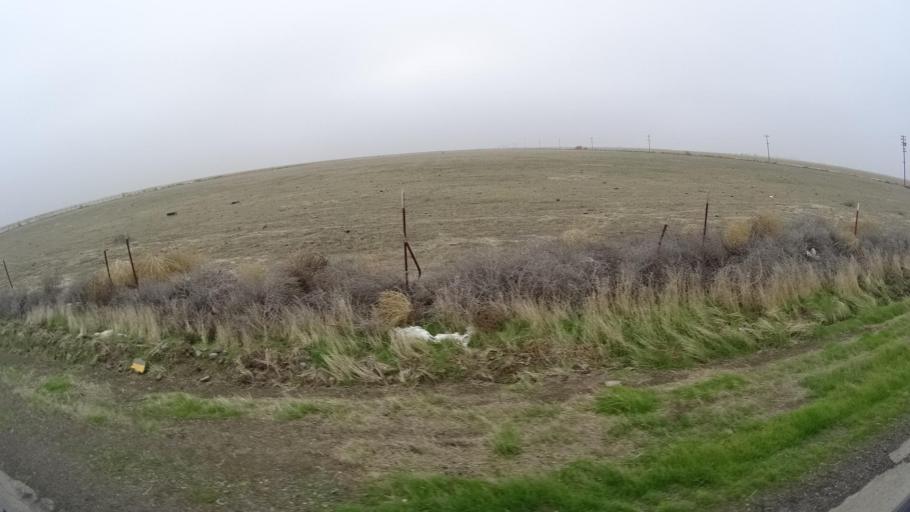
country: US
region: California
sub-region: Tulare County
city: Alpaugh
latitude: 35.7174
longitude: -119.4806
